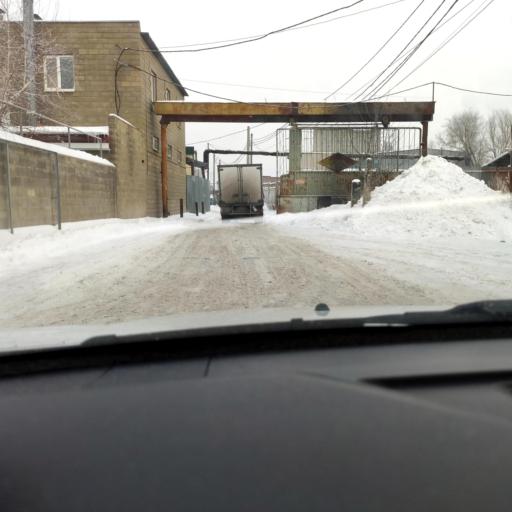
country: RU
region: Samara
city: Samara
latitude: 53.1969
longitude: 50.2664
